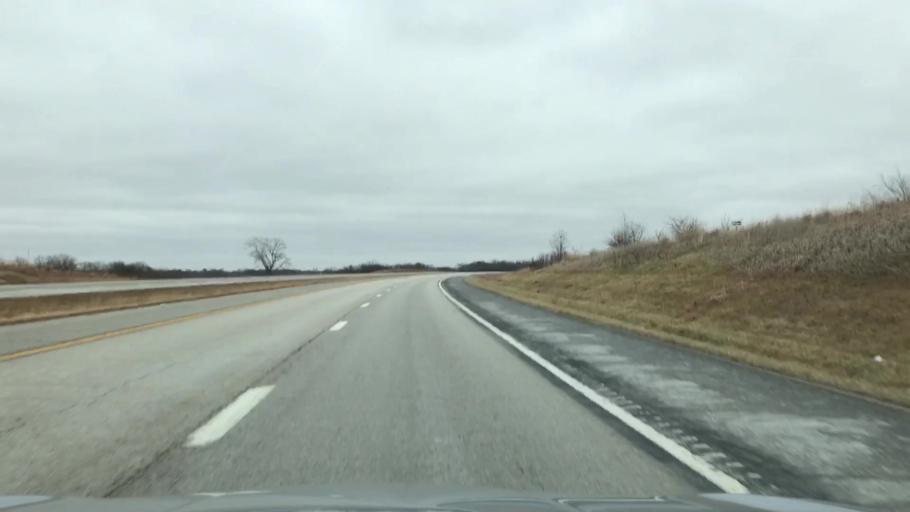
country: US
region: Missouri
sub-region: Caldwell County
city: Hamilton
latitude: 39.7484
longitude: -94.0533
